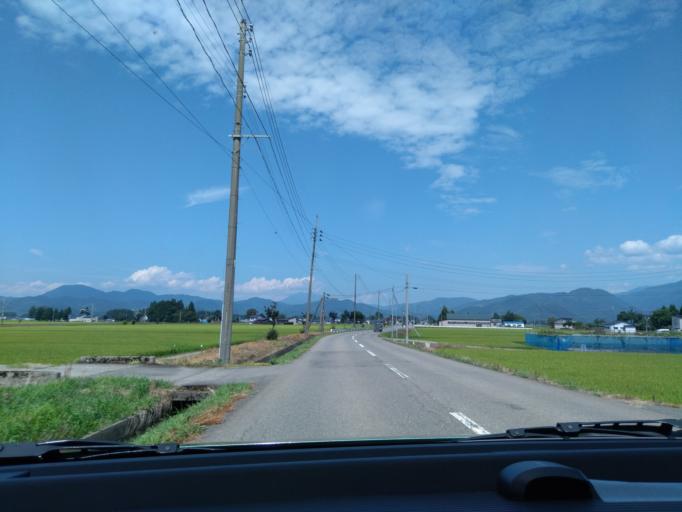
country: JP
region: Akita
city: Kakunodatemachi
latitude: 39.6013
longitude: 140.5829
